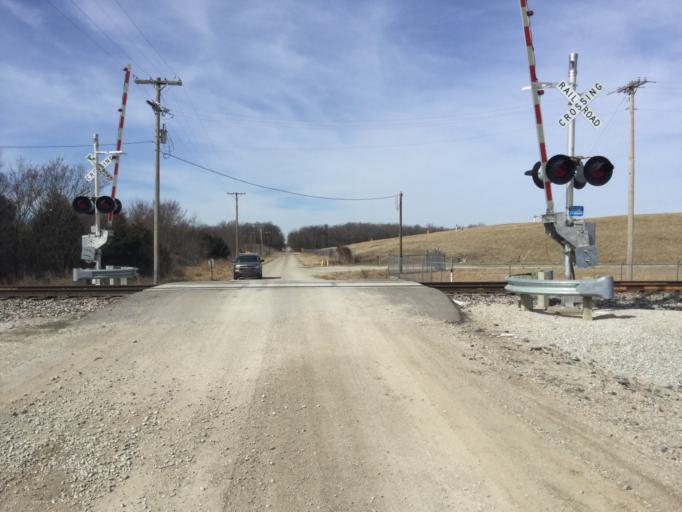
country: US
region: Kansas
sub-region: Cherokee County
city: Columbus
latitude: 37.2371
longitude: -94.8273
